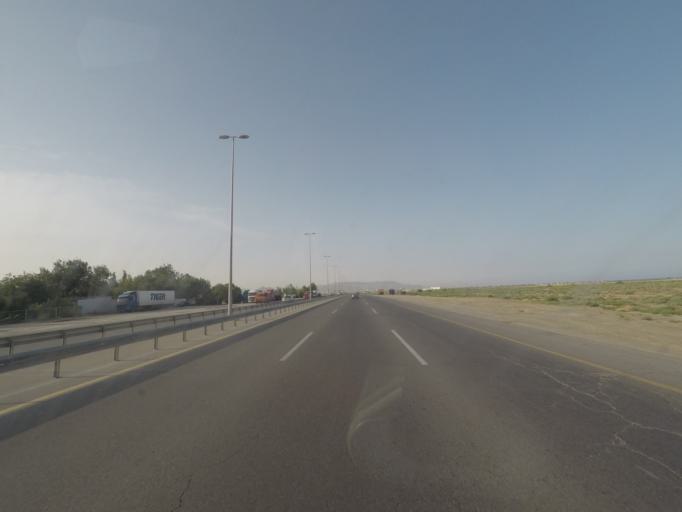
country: AZ
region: Baki
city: Qobustan
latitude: 40.1317
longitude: 49.4438
